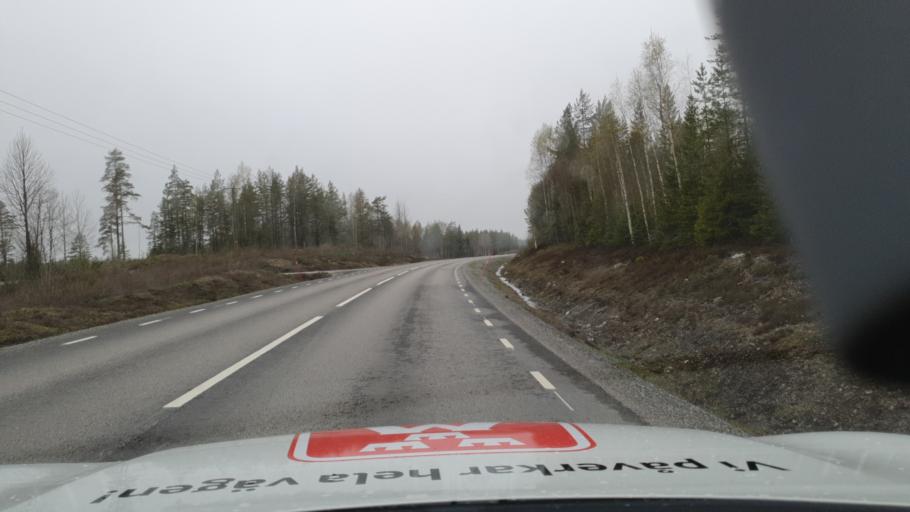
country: SE
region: Vaesterbotten
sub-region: Umea Kommun
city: Hoernefors
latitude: 63.7719
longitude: 19.9723
